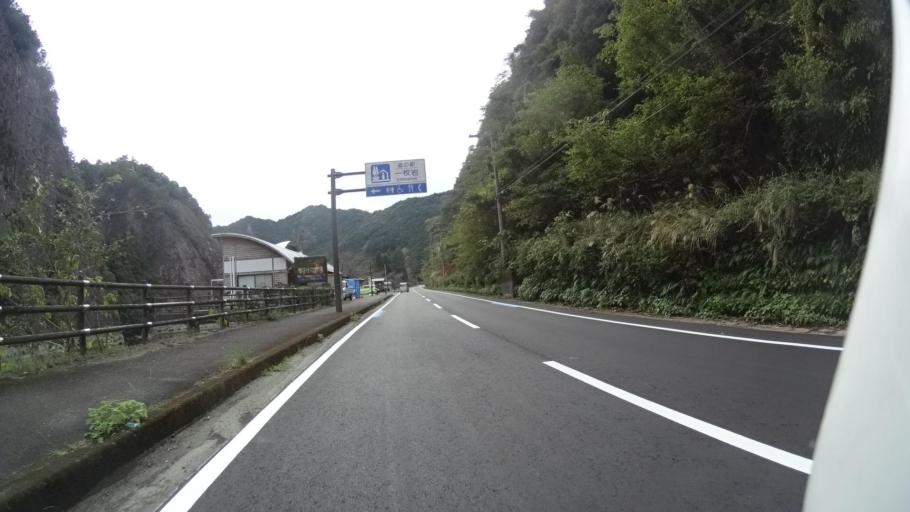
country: JP
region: Wakayama
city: Shingu
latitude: 33.5463
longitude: 135.7197
